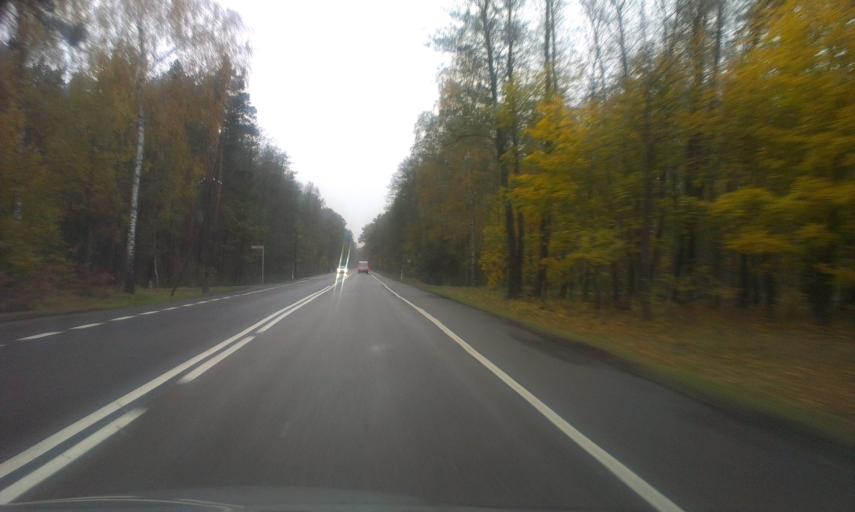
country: PL
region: Greater Poland Voivodeship
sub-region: Powiat chodzieski
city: Budzyn
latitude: 52.8476
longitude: 16.9701
